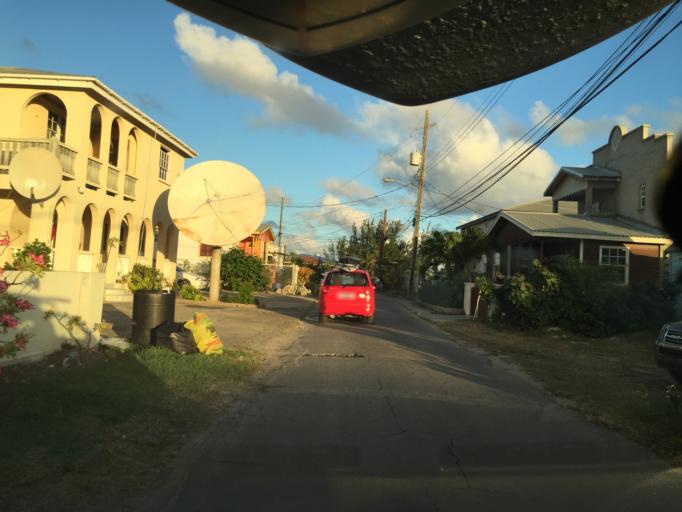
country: BB
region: Christ Church
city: Oistins
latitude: 13.0534
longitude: -59.5091
